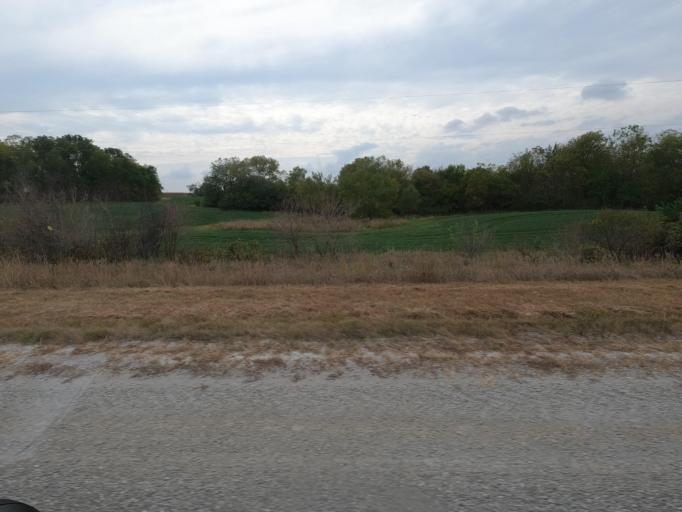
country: US
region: Iowa
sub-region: Jasper County
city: Monroe
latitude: 41.4838
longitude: -93.0610
